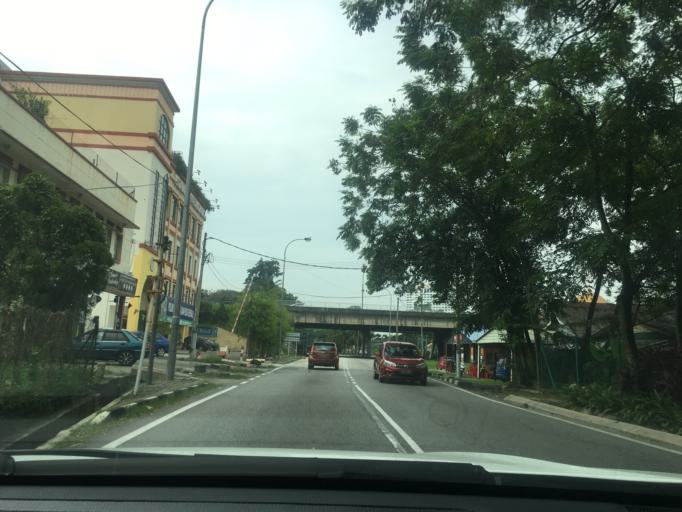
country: MY
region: Selangor
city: Klang
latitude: 3.0441
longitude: 101.4465
